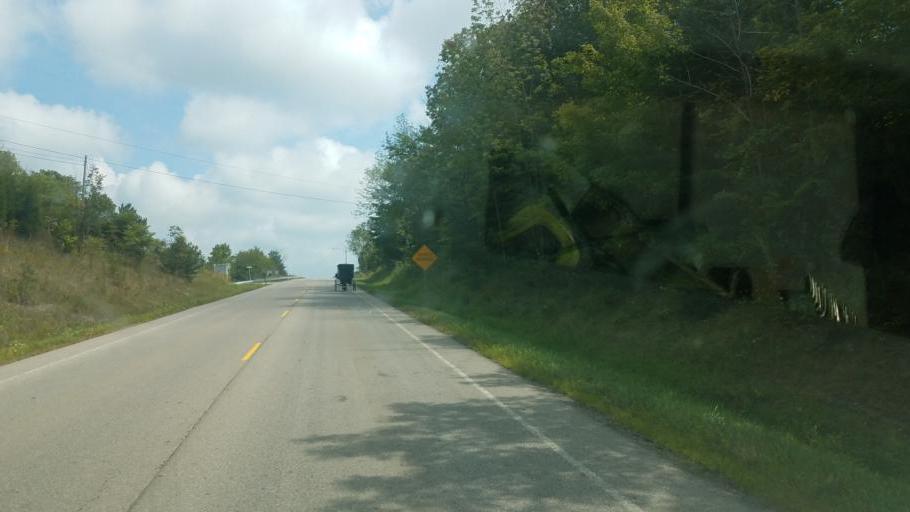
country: US
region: Ohio
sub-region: Licking County
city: Utica
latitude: 40.2346
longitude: -82.4359
